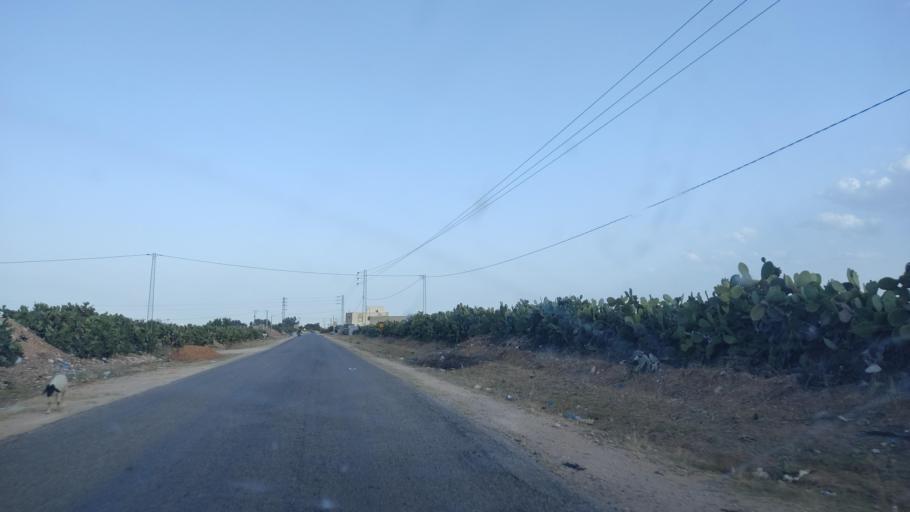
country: TN
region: Safaqis
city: Sfax
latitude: 34.8130
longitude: 10.6592
